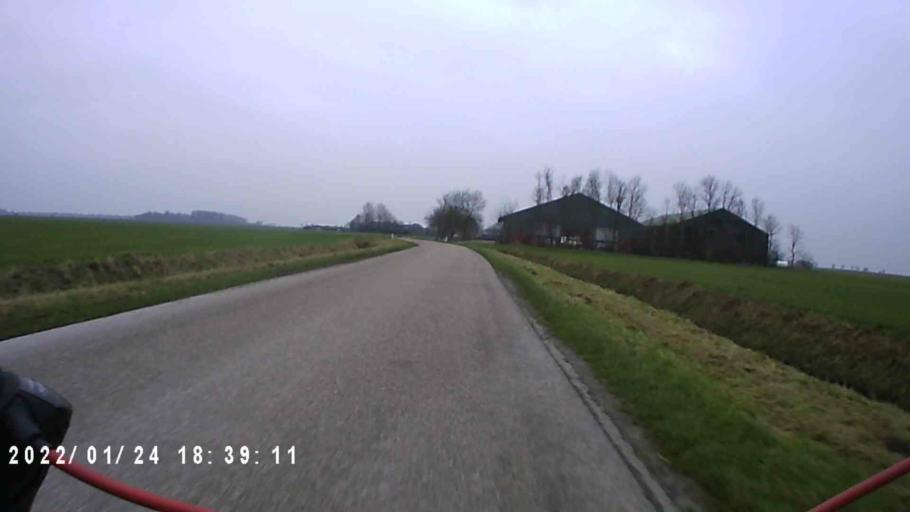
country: NL
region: Groningen
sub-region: Gemeente De Marne
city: Ulrum
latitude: 53.3475
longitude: 6.3387
